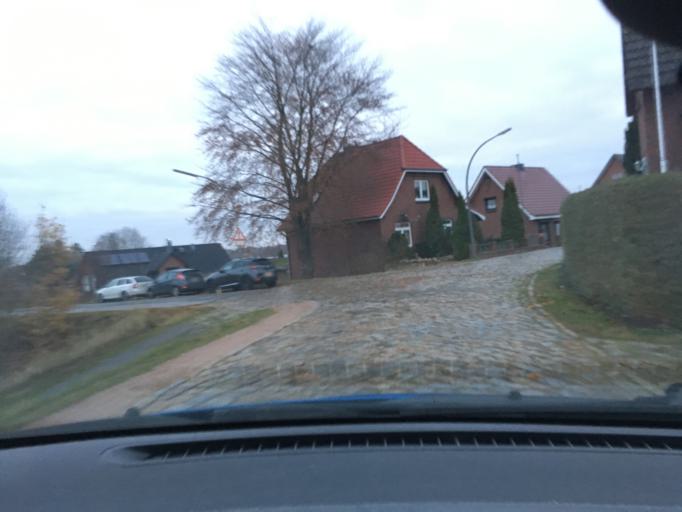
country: DE
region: Lower Saxony
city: Winsen
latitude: 53.3995
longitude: 10.2200
